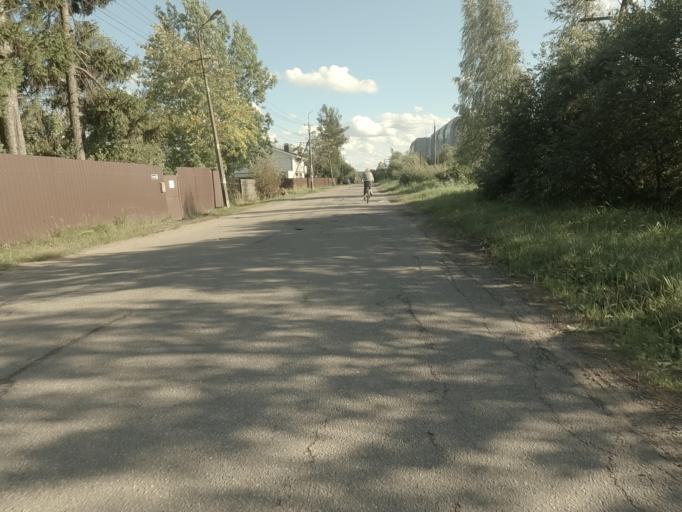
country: RU
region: Leningrad
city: Imeni Morozova
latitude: 59.9619
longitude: 31.0303
